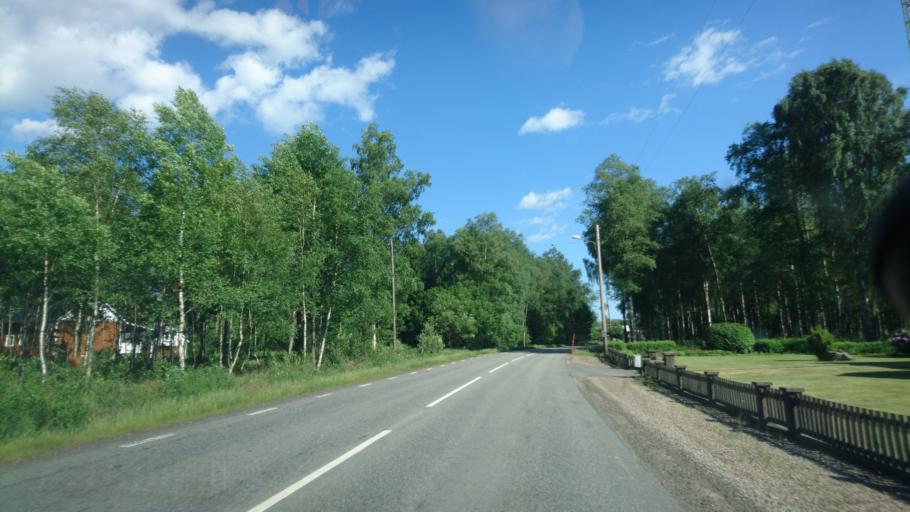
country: SE
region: Kronoberg
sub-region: Almhults Kommun
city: AElmhult
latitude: 56.4748
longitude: 14.2205
